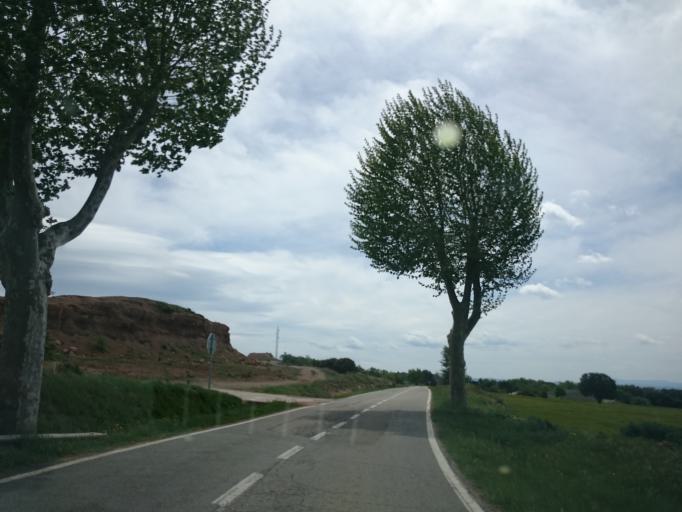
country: ES
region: Catalonia
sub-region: Provincia de Barcelona
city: Prats de Llucanes
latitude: 42.0075
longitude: 2.0393
